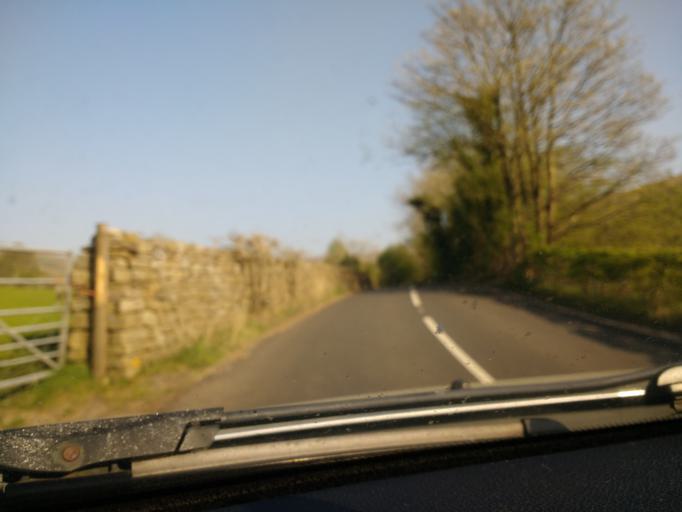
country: GB
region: England
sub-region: Cumbria
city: Sedbergh
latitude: 54.3111
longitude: -2.4376
